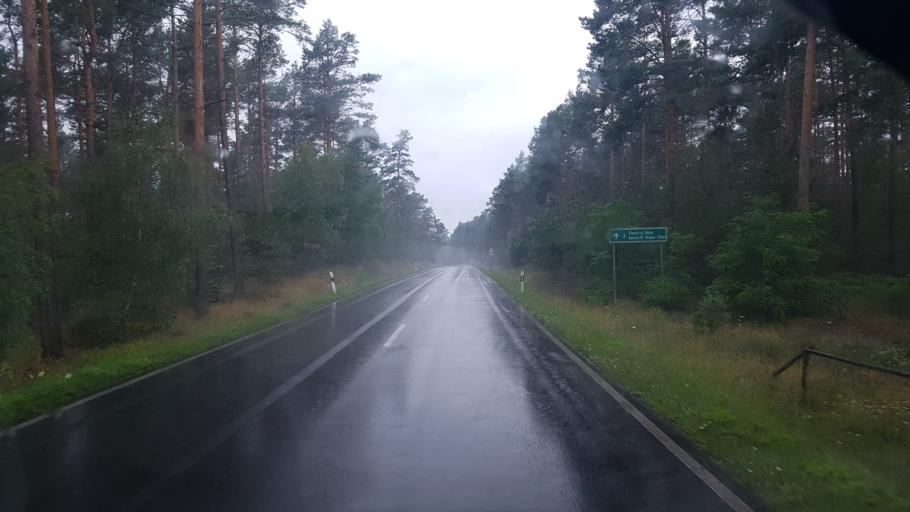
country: DE
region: Brandenburg
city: Teupitz
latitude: 52.0619
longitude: 13.6466
